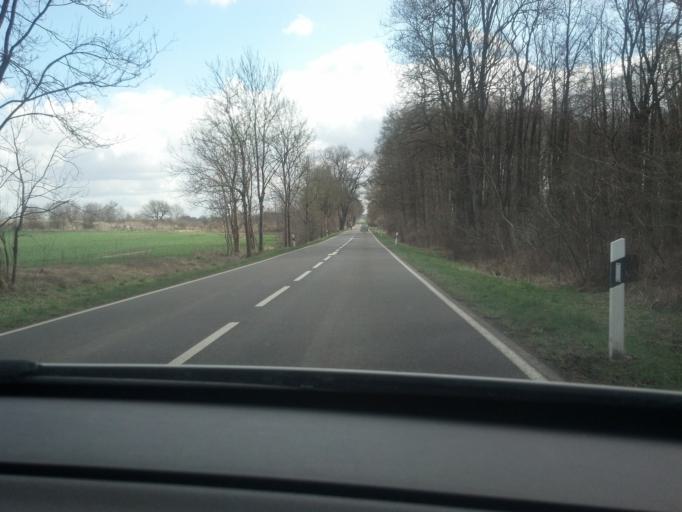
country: DE
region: Mecklenburg-Vorpommern
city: Loitz
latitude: 53.3764
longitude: 13.3548
